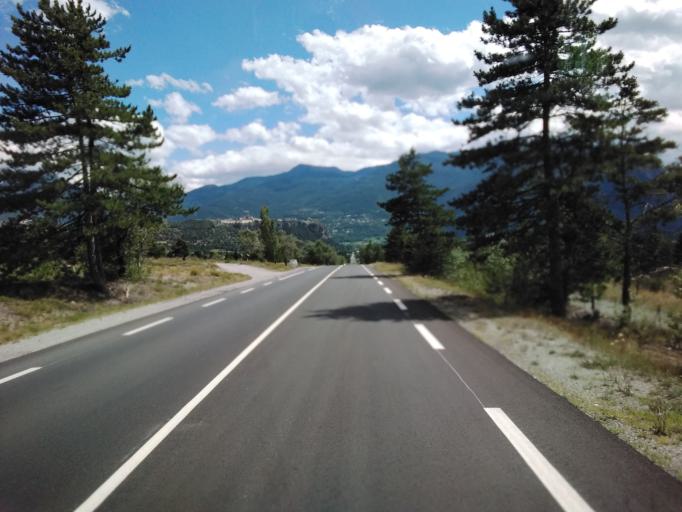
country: FR
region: Provence-Alpes-Cote d'Azur
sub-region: Departement des Hautes-Alpes
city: Guillestre
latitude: 44.6904
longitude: 6.6126
